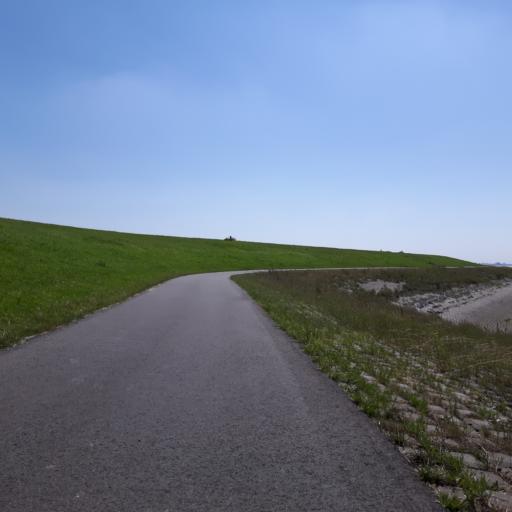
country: NL
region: Zeeland
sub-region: Gemeente Reimerswaal
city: Yerseke
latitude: 51.4353
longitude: 4.0343
